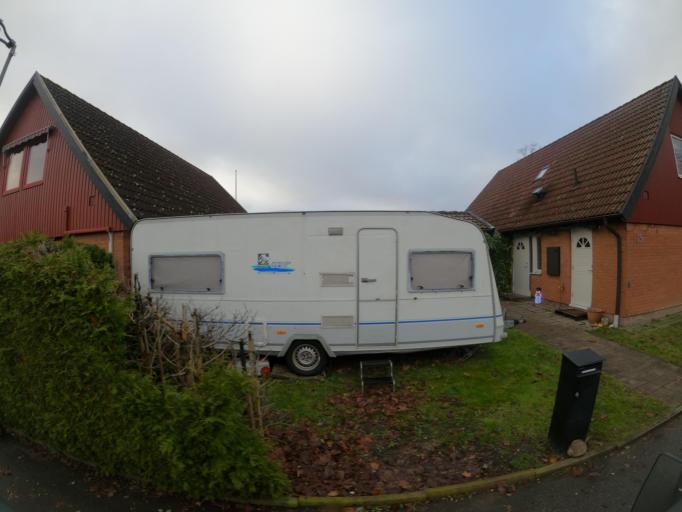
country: SE
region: Skane
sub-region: Svedala Kommun
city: Svedala
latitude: 55.5236
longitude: 13.2110
